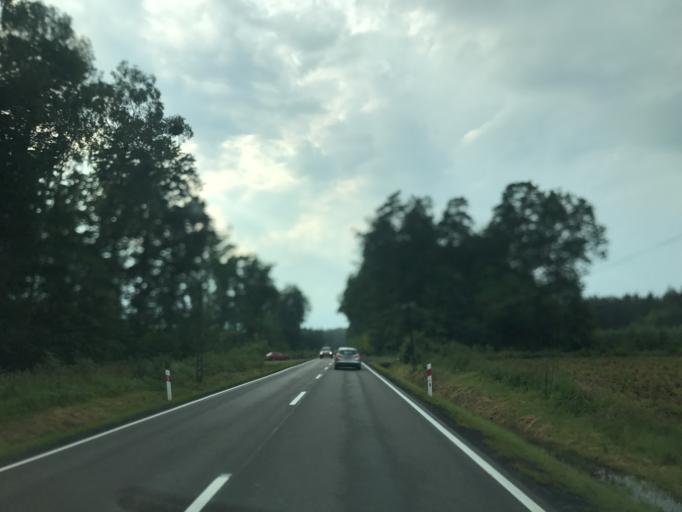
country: PL
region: Pomeranian Voivodeship
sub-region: Powiat czluchowski
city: Czluchow
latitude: 53.6944
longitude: 17.2983
